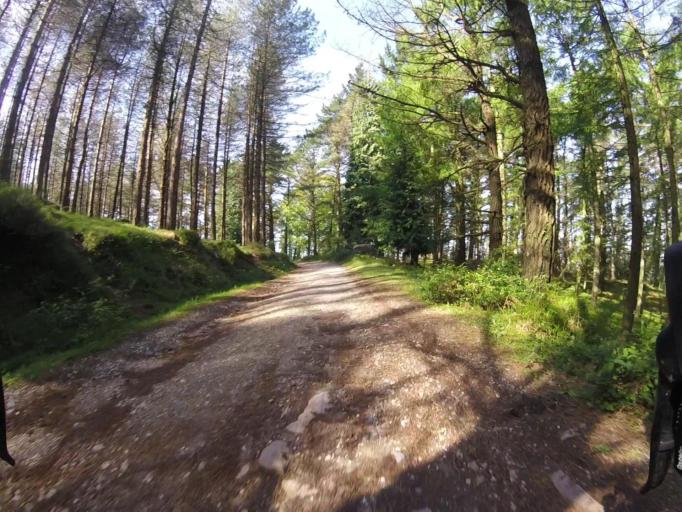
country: ES
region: Basque Country
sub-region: Provincia de Guipuzcoa
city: Andoain
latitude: 43.2033
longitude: -1.9928
